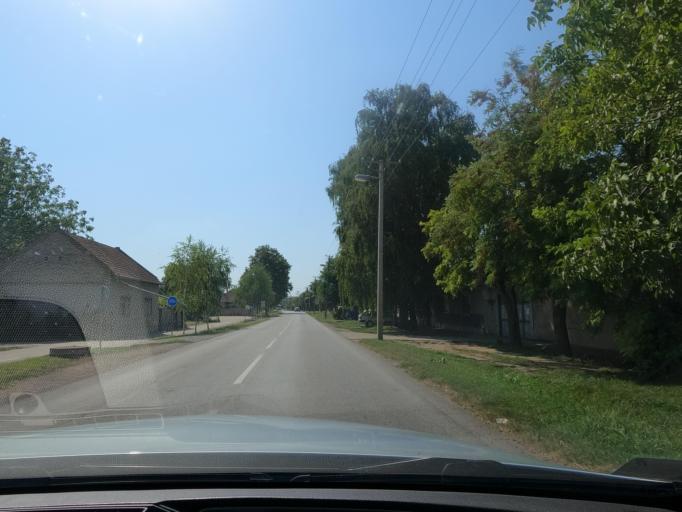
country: RS
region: Autonomna Pokrajina Vojvodina
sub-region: Severnobacki Okrug
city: Backa Topola
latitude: 45.8205
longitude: 19.6552
